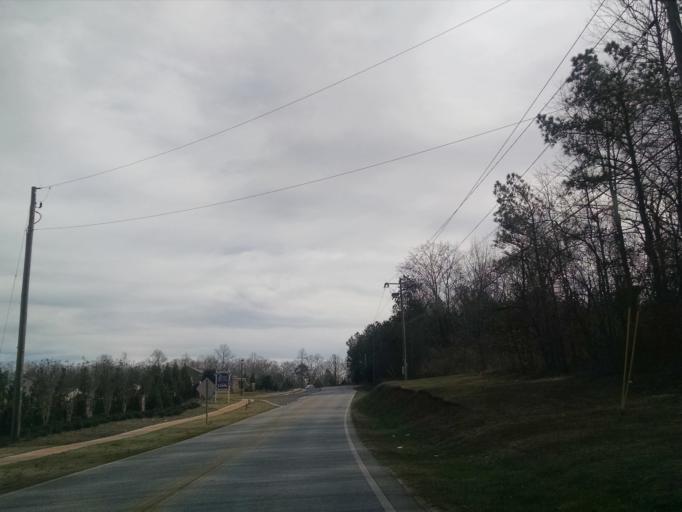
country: US
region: Georgia
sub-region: Gwinnett County
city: Sugar Hill
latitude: 34.0665
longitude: -84.0075
